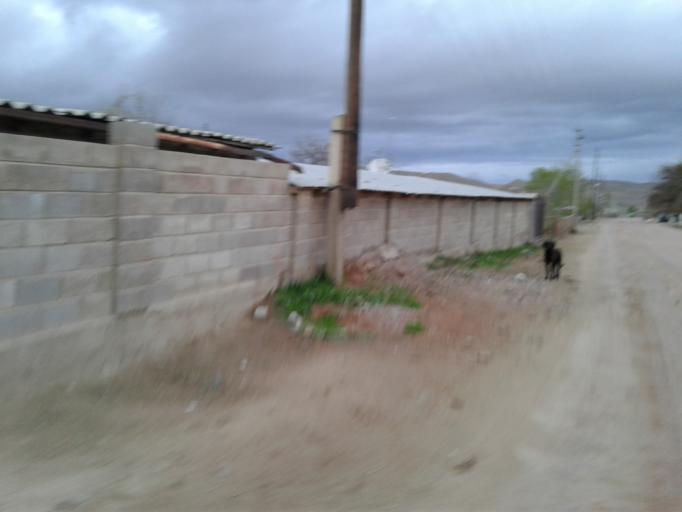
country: KG
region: Ysyk-Koel
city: Bokombayevskoye
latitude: 42.1168
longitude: 76.9878
